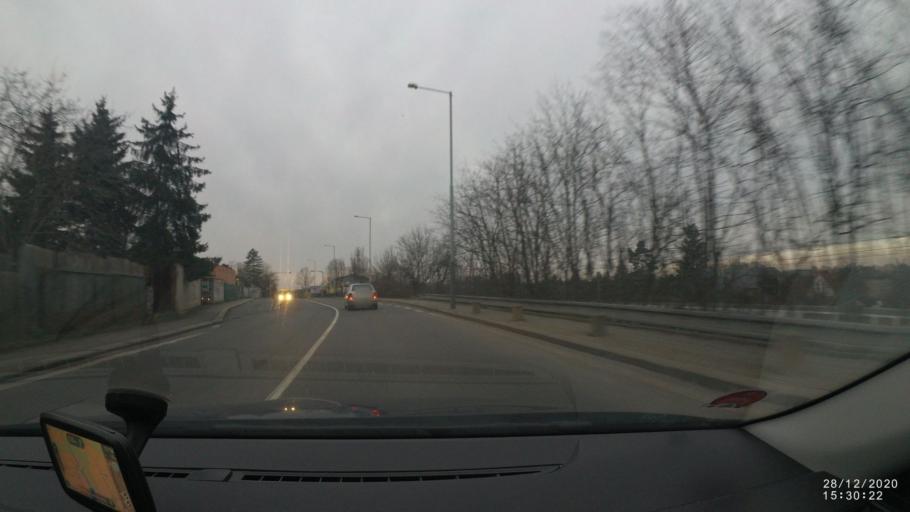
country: CZ
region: Praha
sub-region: Praha 14
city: Dolni Pocernice
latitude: 50.0870
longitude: 14.5726
